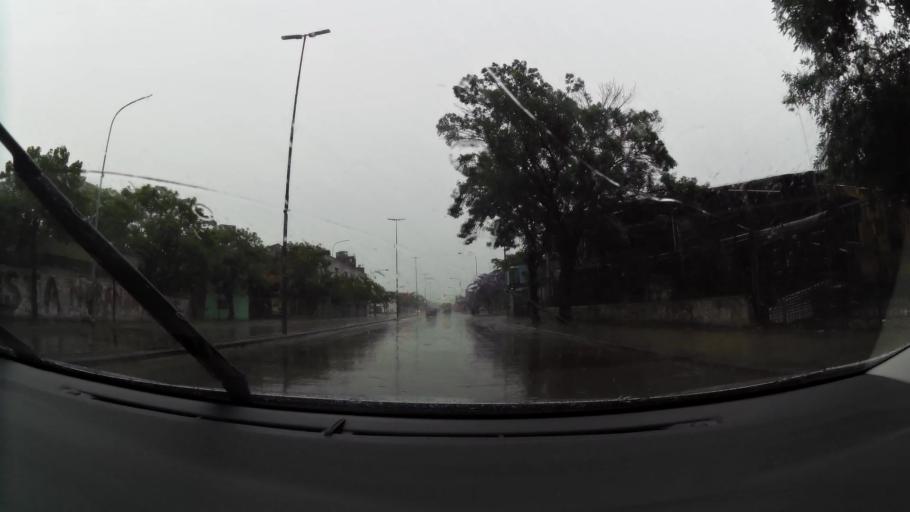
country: AR
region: Buenos Aires F.D.
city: Villa Lugano
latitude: -34.6500
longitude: -58.4237
